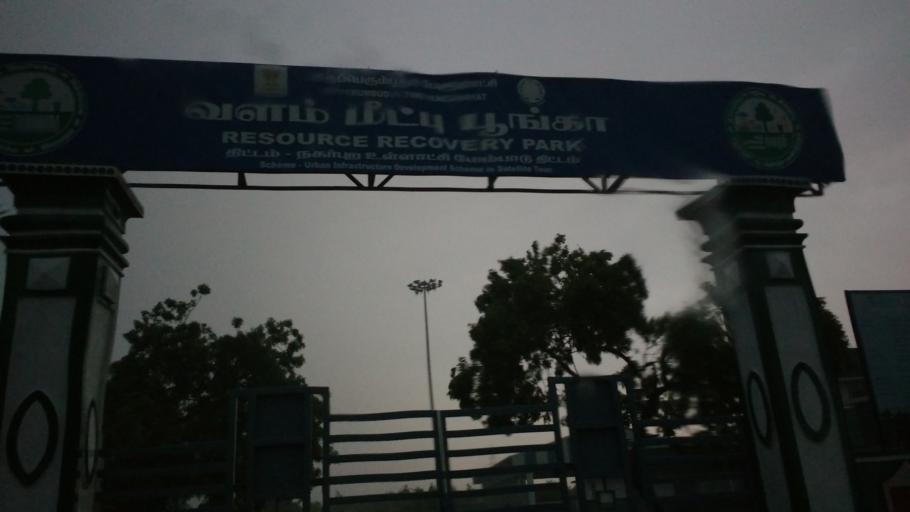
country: IN
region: Tamil Nadu
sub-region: Kancheepuram
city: Sriperumbudur
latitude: 12.9821
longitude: 79.9315
